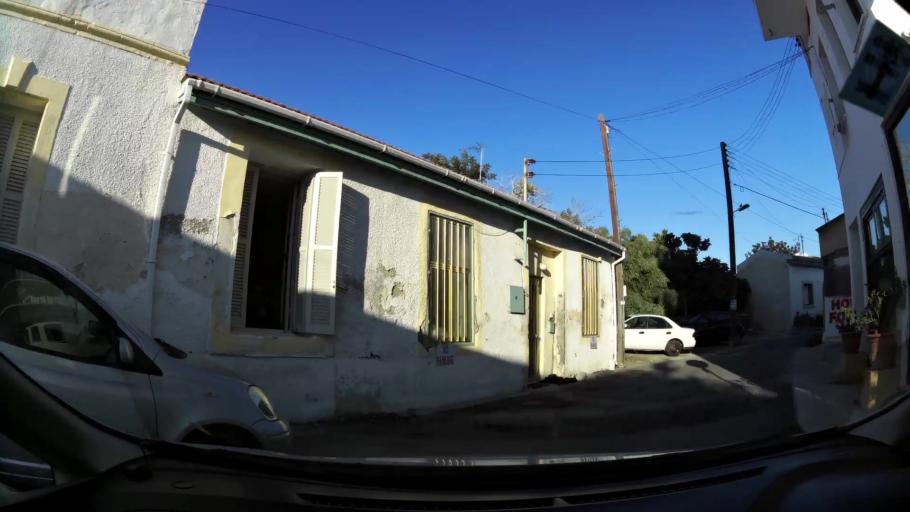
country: CY
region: Larnaka
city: Larnaca
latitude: 34.9090
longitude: 33.6150
